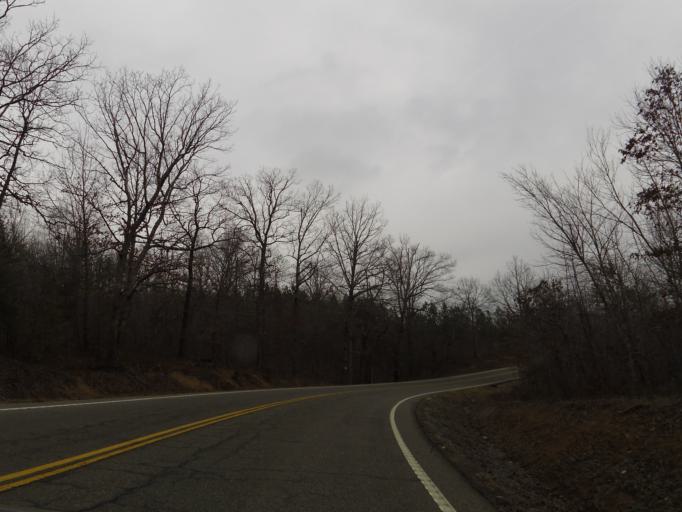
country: US
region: Tennessee
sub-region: Scott County
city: Huntsville
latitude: 36.2988
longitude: -84.6477
